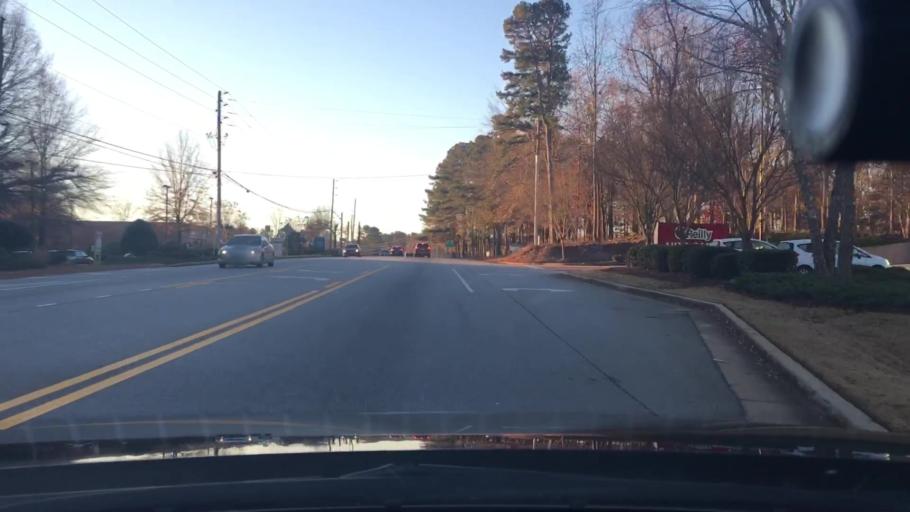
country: US
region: Georgia
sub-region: Fayette County
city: Peachtree City
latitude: 33.4110
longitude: -84.6827
